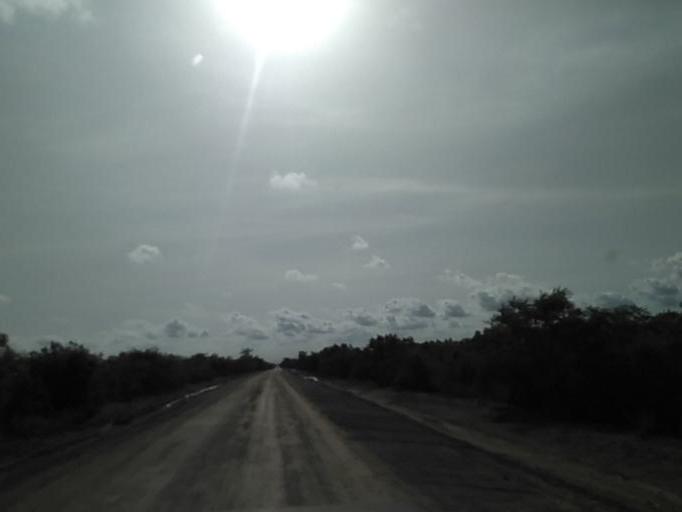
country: GH
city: Akropong
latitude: 6.0362
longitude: 0.3126
